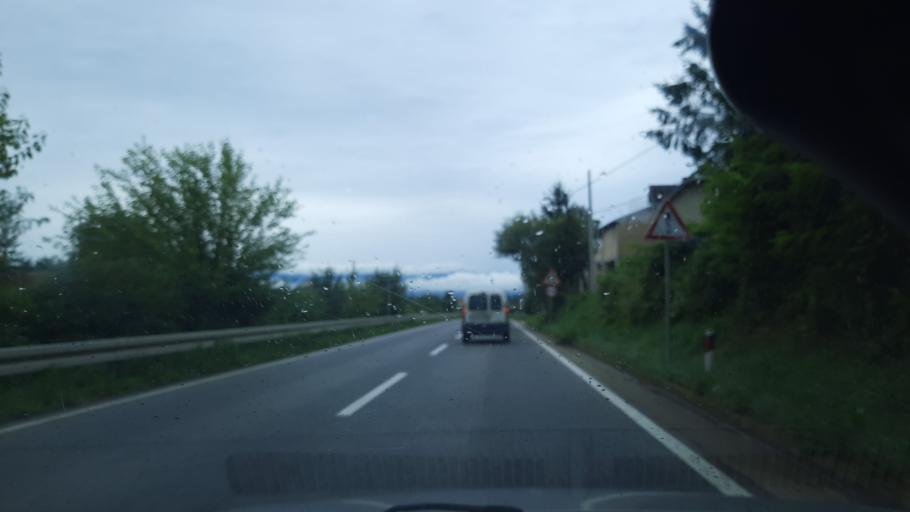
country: RS
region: Central Serbia
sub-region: Raski Okrug
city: Kraljevo
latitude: 43.7614
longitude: 20.8055
